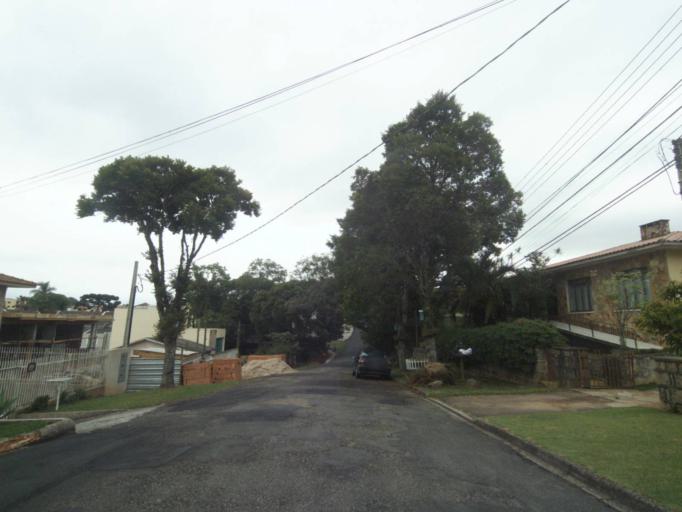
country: BR
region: Parana
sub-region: Curitiba
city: Curitiba
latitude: -25.4147
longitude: -49.2940
